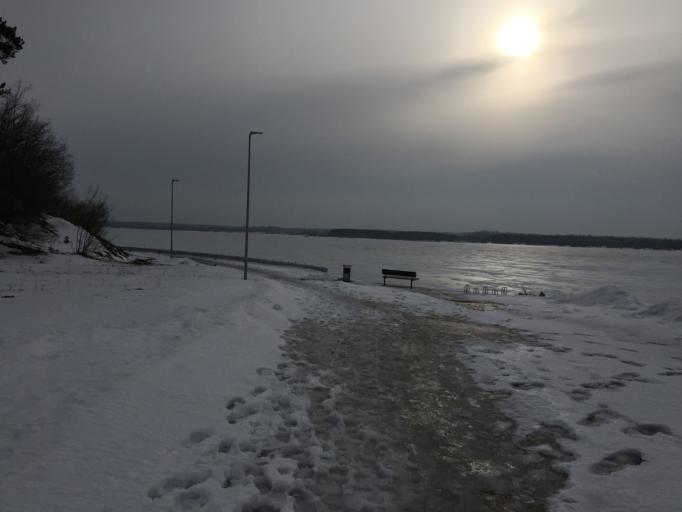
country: LV
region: Ikskile
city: Ikskile
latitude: 56.8440
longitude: 24.4527
